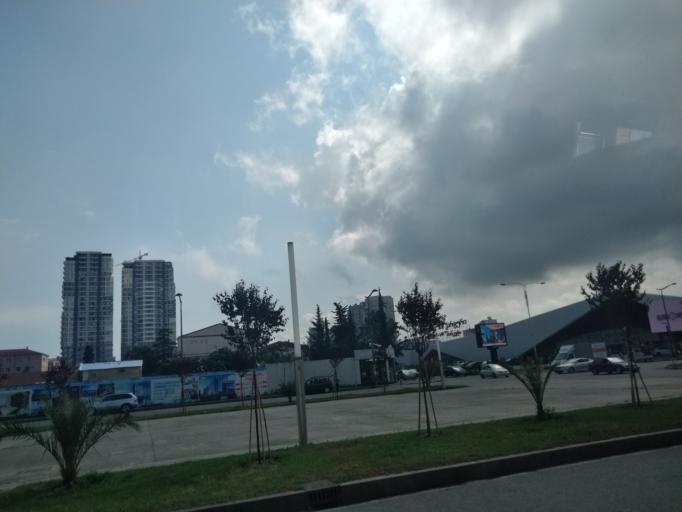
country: GE
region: Ajaria
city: Batumi
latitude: 41.6374
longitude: 41.6182
